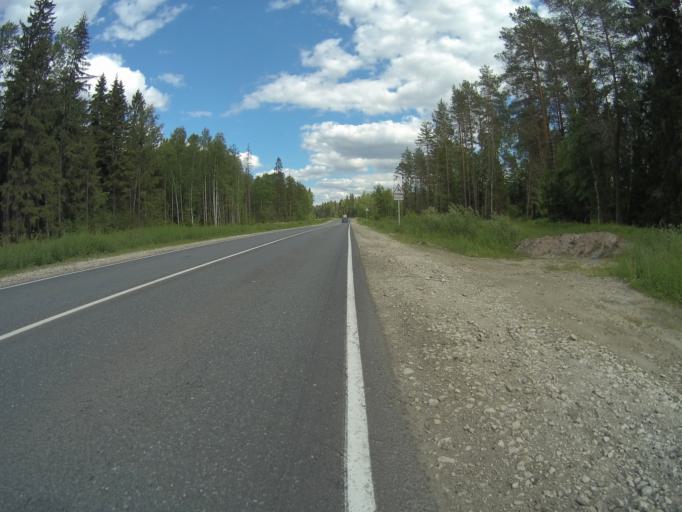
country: RU
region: Vladimir
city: Orgtrud
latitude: 56.0115
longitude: 40.6028
